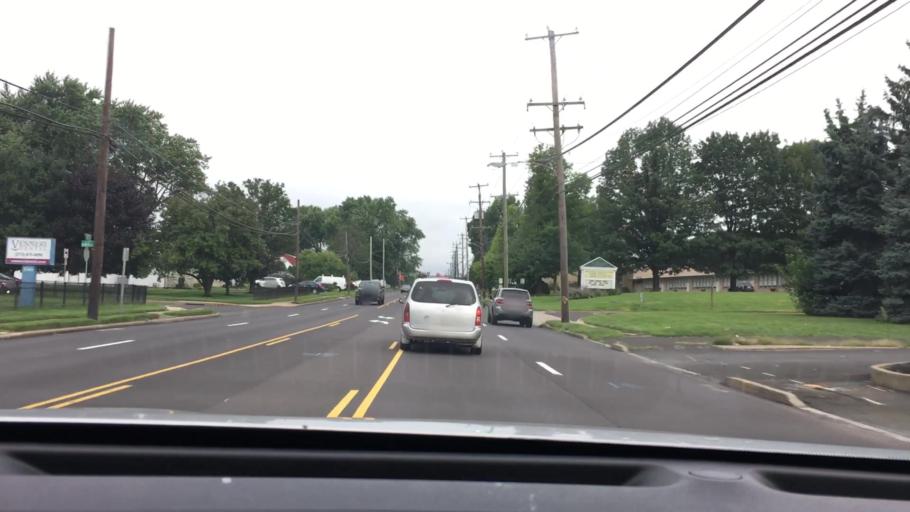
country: US
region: Pennsylvania
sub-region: Bucks County
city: Warminster Heights
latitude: 40.1806
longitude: -75.0871
